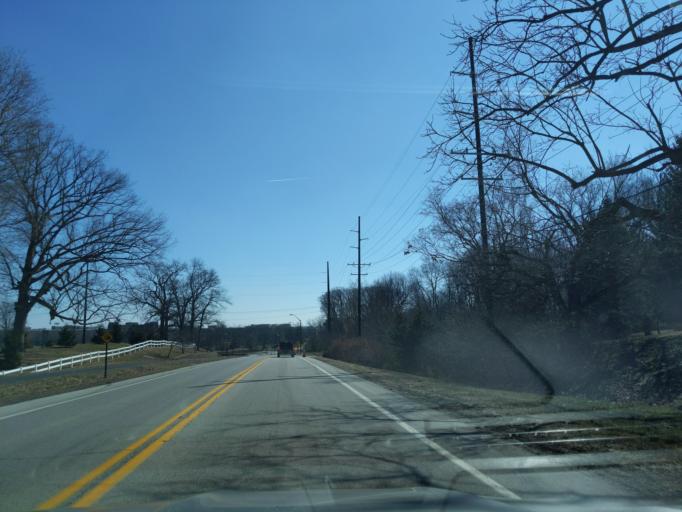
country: US
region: Indiana
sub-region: Tippecanoe County
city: West Lafayette
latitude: 40.4327
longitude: -86.9337
